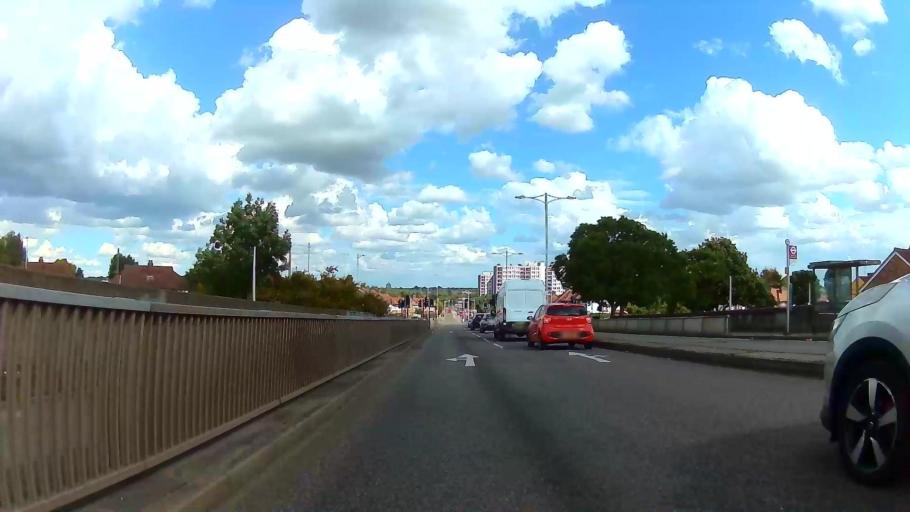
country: GB
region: England
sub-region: Greater London
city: Woodford Green
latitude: 51.6031
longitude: 0.0338
